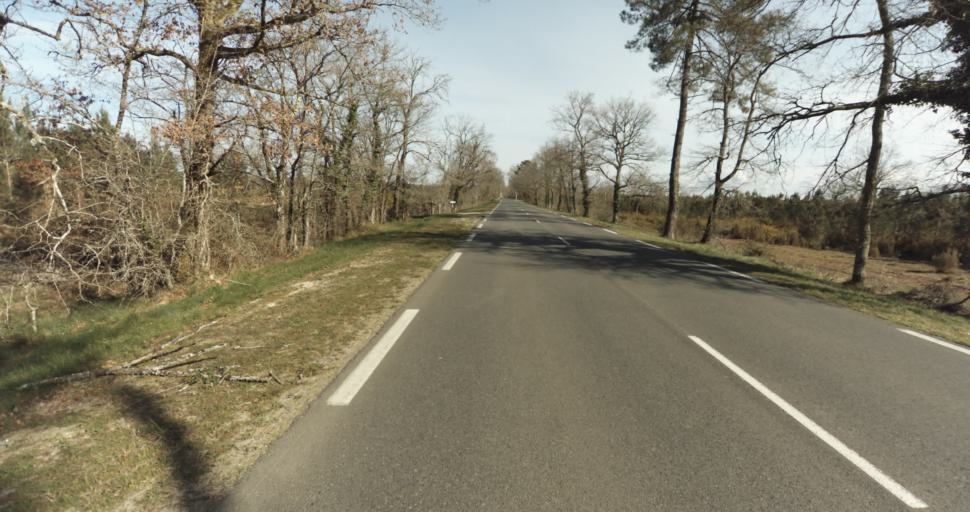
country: FR
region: Aquitaine
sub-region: Departement des Landes
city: Roquefort
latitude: 44.0761
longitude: -0.3132
